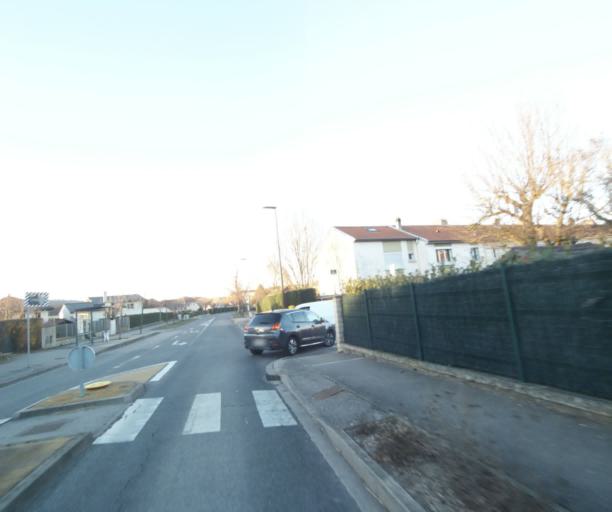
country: FR
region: Lorraine
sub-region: Departement de Meurthe-et-Moselle
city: Pulnoy
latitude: 48.6969
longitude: 6.2549
